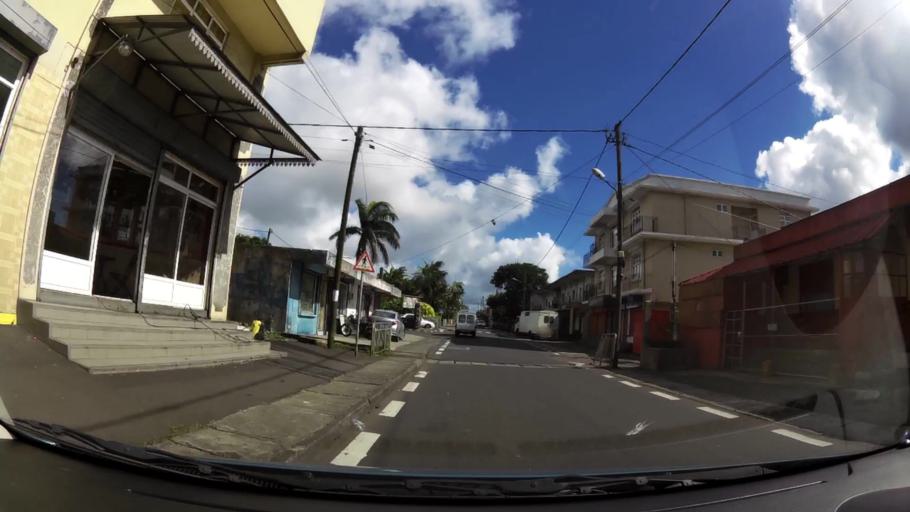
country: MU
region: Plaines Wilhems
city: Curepipe
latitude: -20.3304
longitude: 57.5250
